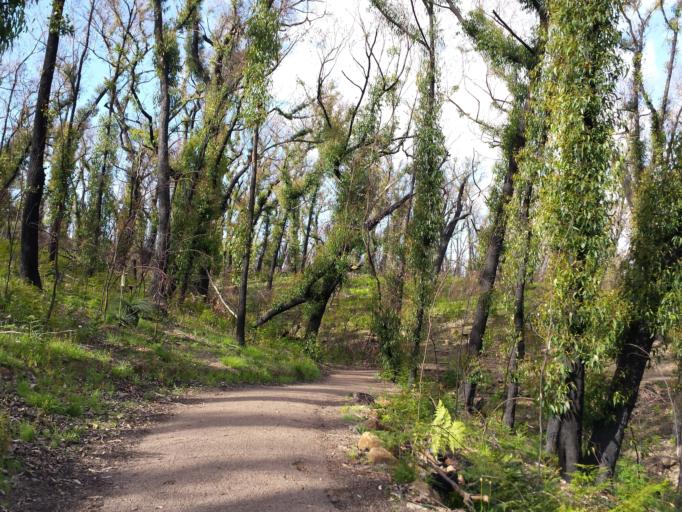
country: AU
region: Victoria
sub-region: Northern Grampians
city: Stawell
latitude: -37.1089
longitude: 142.4075
